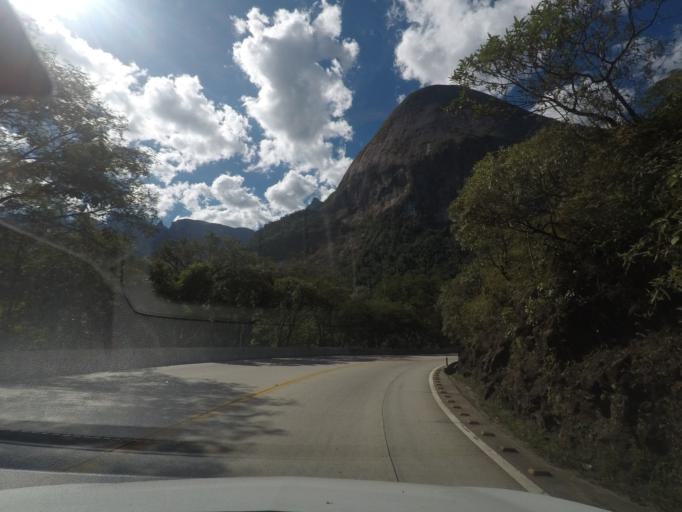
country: BR
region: Rio de Janeiro
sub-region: Guapimirim
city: Guapimirim
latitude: -22.4886
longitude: -42.9992
